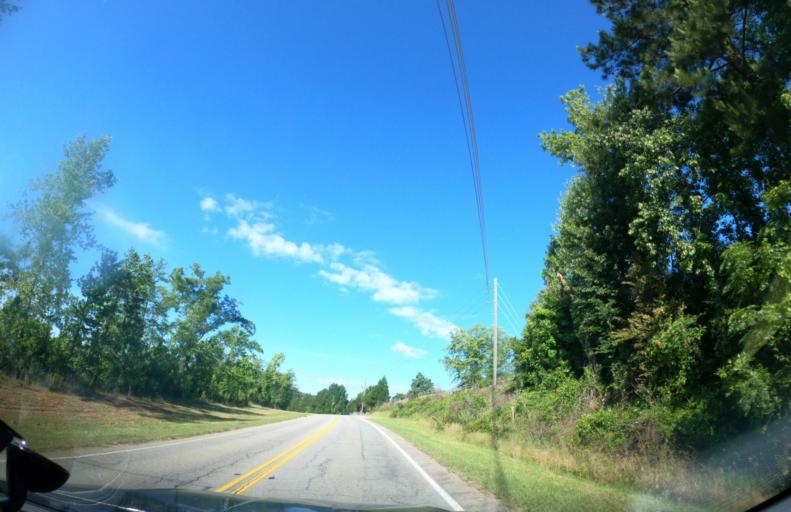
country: US
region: Georgia
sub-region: Columbia County
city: Grovetown
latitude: 33.4561
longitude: -82.2369
